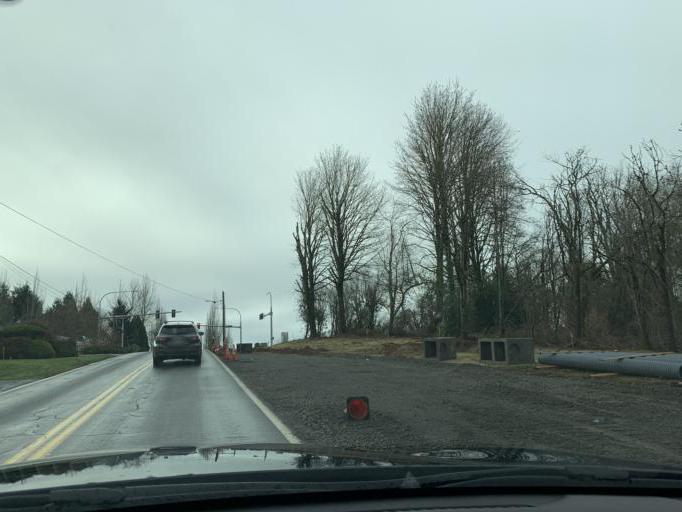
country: US
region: Washington
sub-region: Clark County
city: Camas
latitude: 45.5916
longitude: -122.4527
